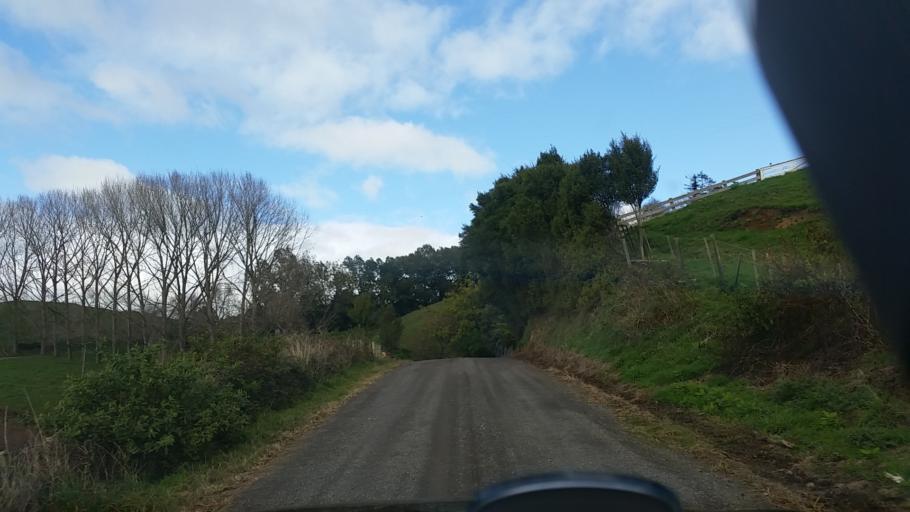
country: NZ
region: Waikato
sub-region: Matamata-Piako District
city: Matamata
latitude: -37.8240
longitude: 175.6756
